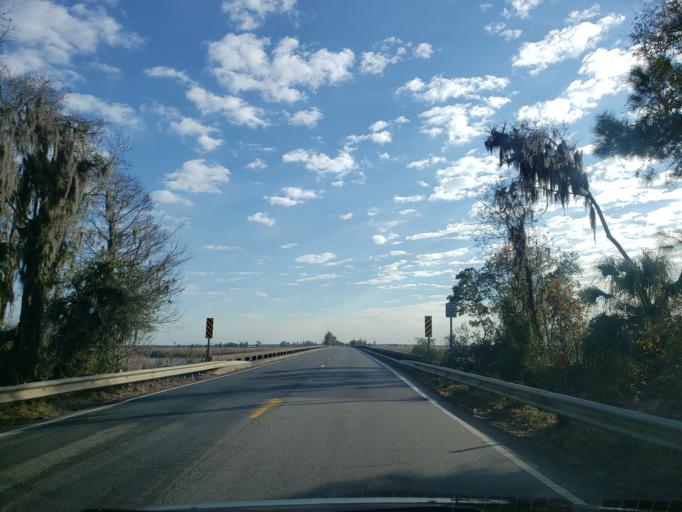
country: US
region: Georgia
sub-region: Chatham County
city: Port Wentworth
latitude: 32.1657
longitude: -81.1397
